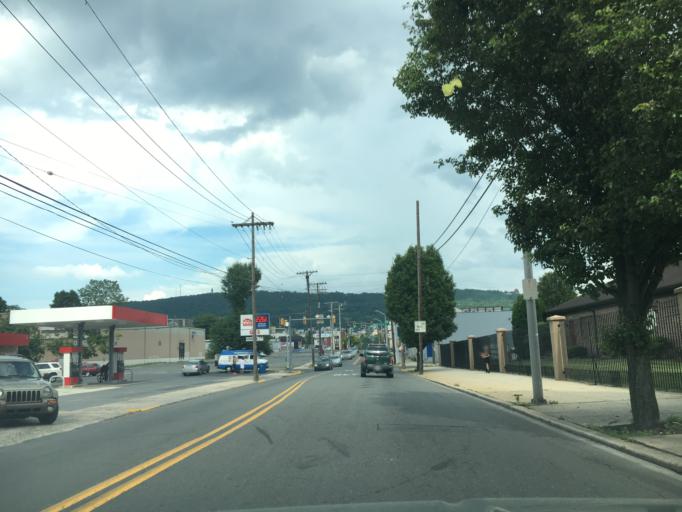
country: US
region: Pennsylvania
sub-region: Berks County
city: Reading
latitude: 40.3416
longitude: -75.9325
